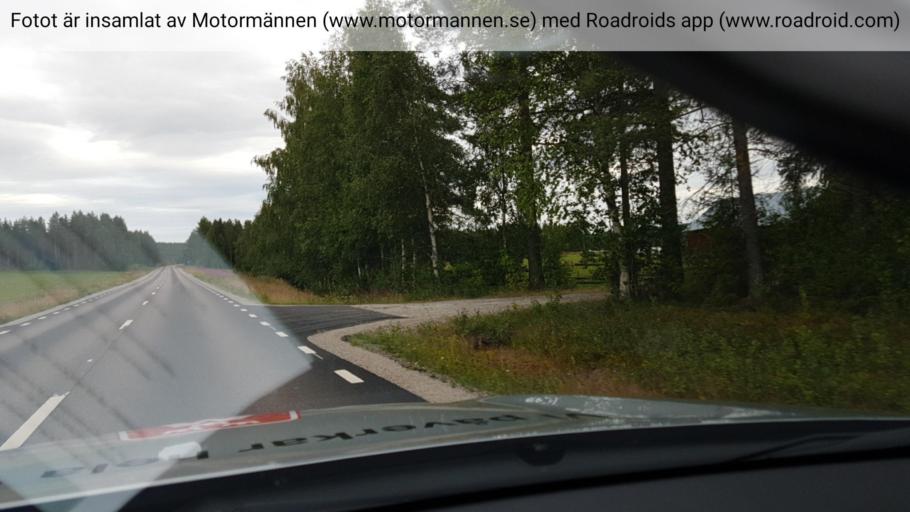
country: SE
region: Norrbotten
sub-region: Overkalix Kommun
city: OEverkalix
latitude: 66.4242
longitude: 22.7980
